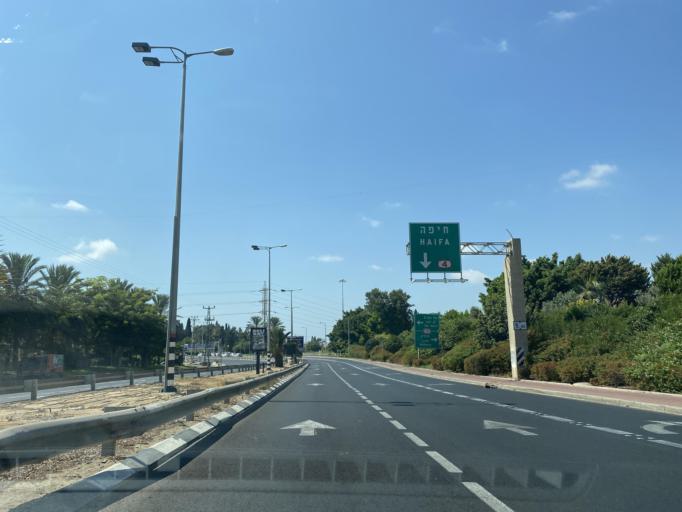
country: IL
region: Central District
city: Kfar Saba
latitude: 32.1763
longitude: 34.8905
